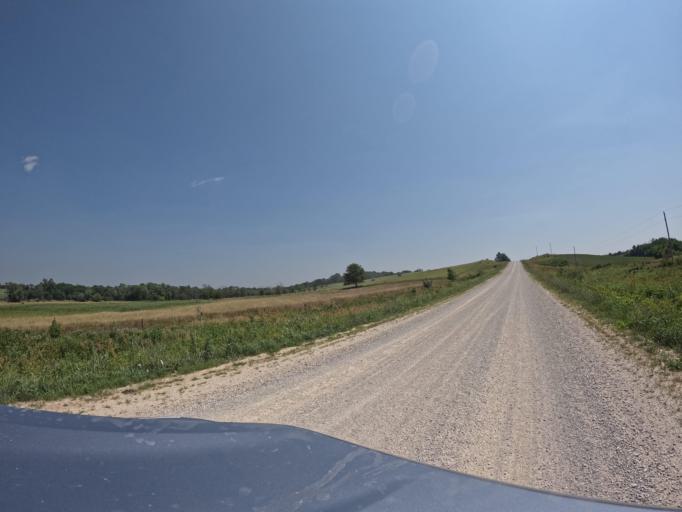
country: US
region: Iowa
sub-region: Keokuk County
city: Sigourney
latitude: 41.3486
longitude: -92.2389
